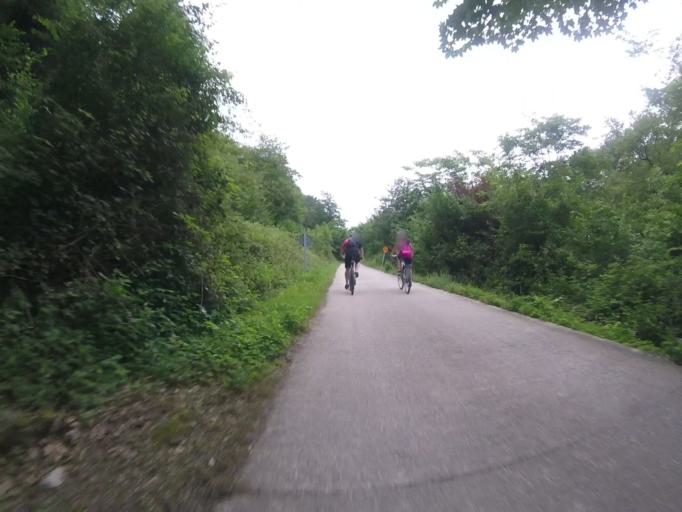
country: ES
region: Navarre
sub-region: Provincia de Navarra
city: Sunbilla
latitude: 43.1568
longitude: -1.6716
